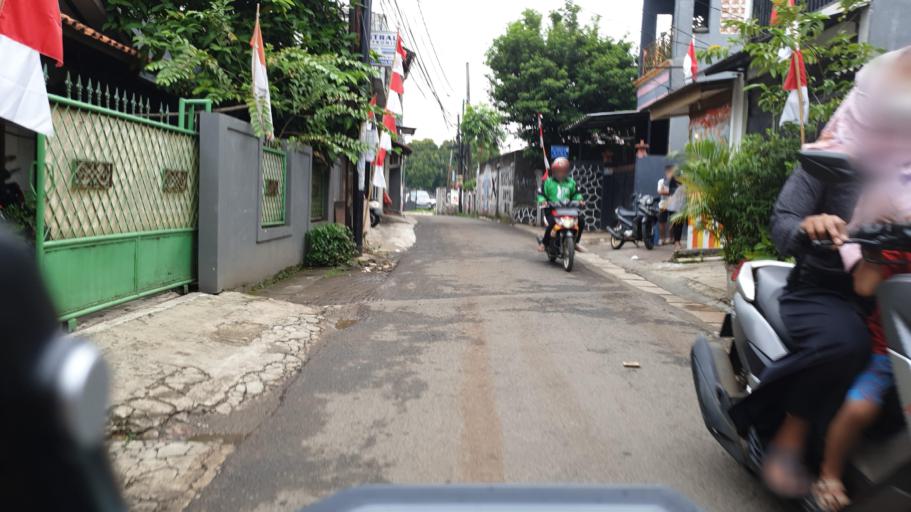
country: ID
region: West Java
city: Pamulang
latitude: -6.3348
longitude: 106.7697
